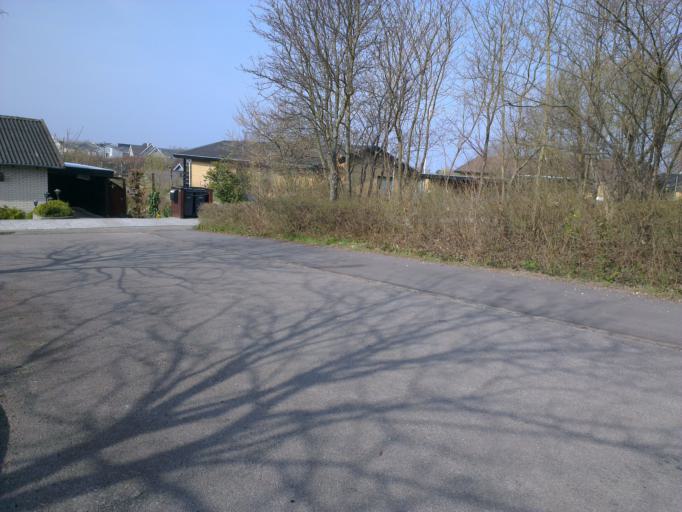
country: DK
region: Capital Region
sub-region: Frederikssund Kommune
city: Frederikssund
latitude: 55.8187
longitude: 12.0875
